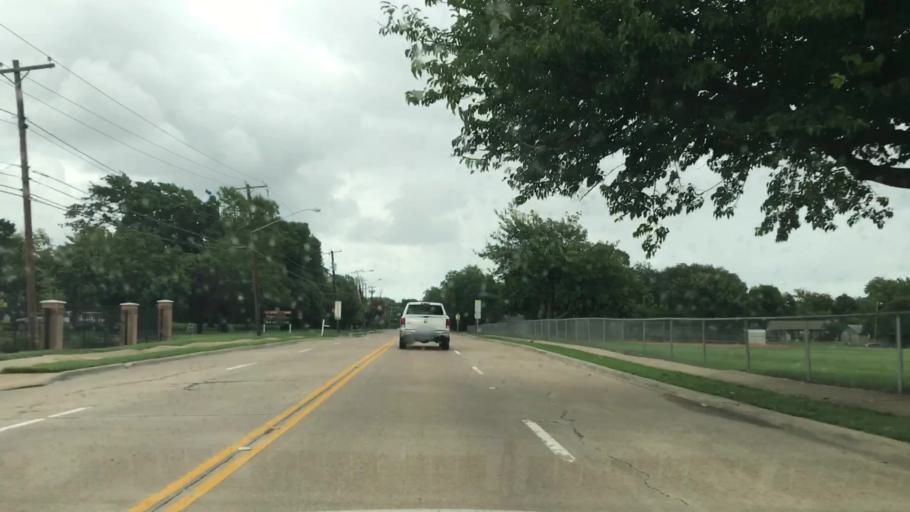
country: US
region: Texas
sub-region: Dallas County
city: Richardson
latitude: 32.9048
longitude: -96.7526
